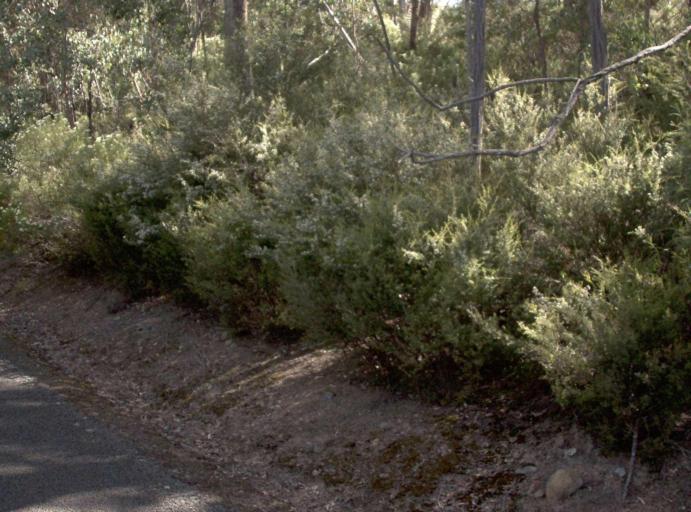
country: AU
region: Victoria
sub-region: East Gippsland
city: Lakes Entrance
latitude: -37.4822
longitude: 148.1263
